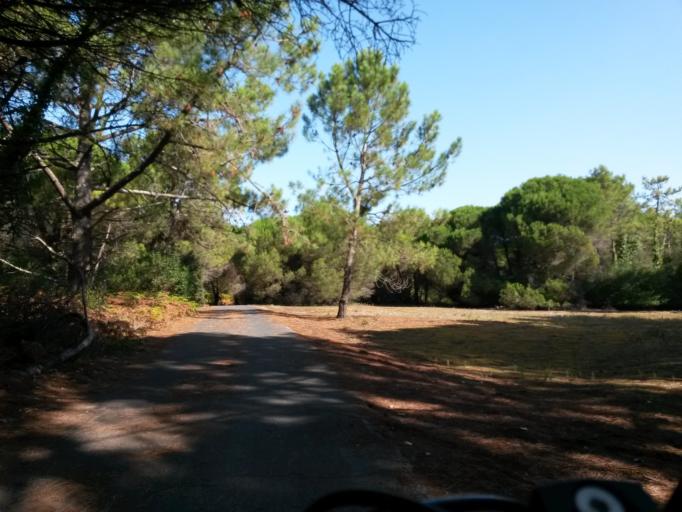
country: FR
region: Poitou-Charentes
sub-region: Departement de la Charente-Maritime
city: Le Bois-Plage-en-Re
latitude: 46.1768
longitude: -1.3703
